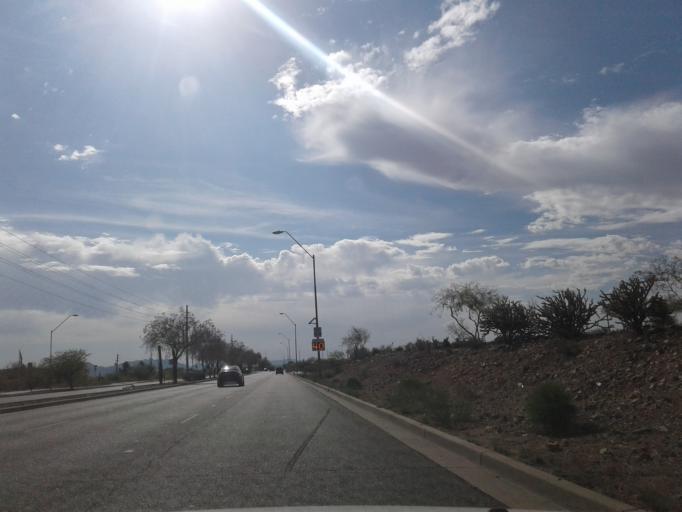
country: US
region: Arizona
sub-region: Maricopa County
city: Fountain Hills
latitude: 33.5826
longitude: -111.8143
